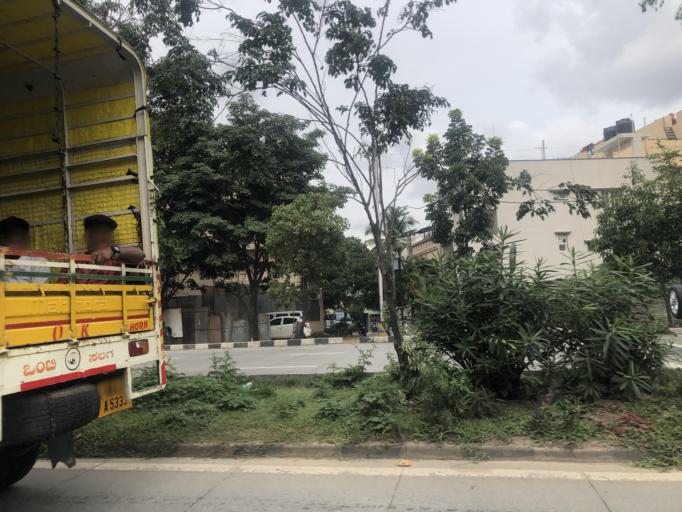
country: IN
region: Karnataka
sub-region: Bangalore Urban
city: Bangalore
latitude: 12.9790
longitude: 77.5153
